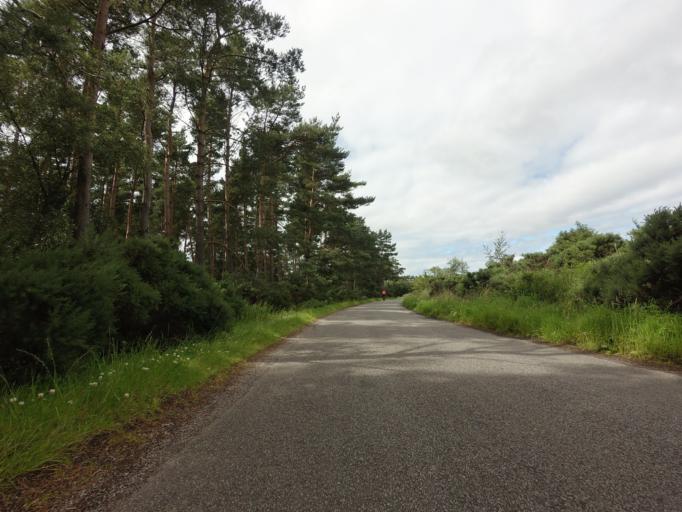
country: GB
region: Scotland
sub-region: Moray
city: Kinloss
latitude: 57.6284
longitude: -3.5914
